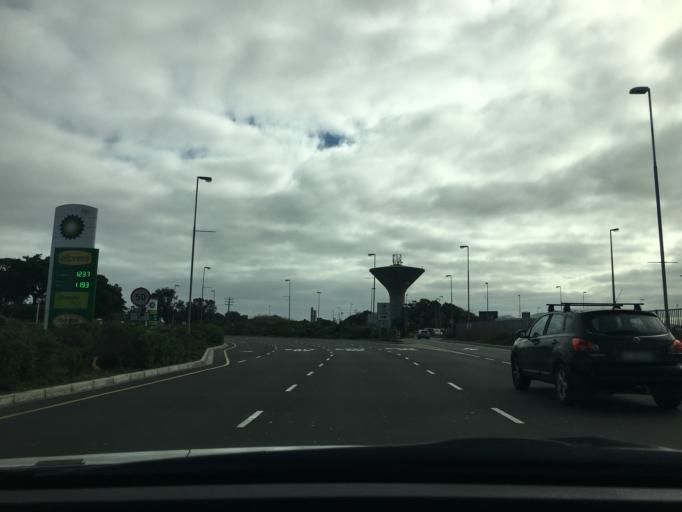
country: ZA
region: Western Cape
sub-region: City of Cape Town
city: Lansdowne
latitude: -33.9703
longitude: 18.5928
